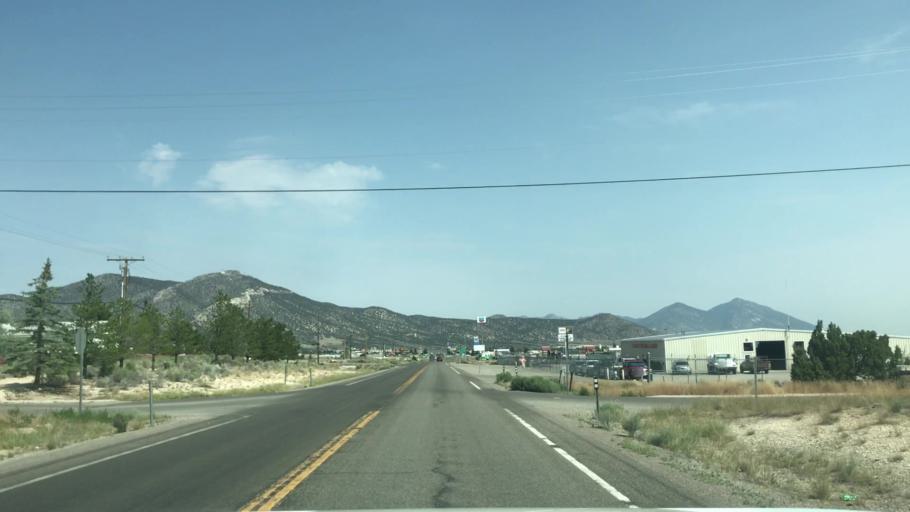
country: US
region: Nevada
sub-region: White Pine County
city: Ely
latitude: 39.2319
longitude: -114.8629
